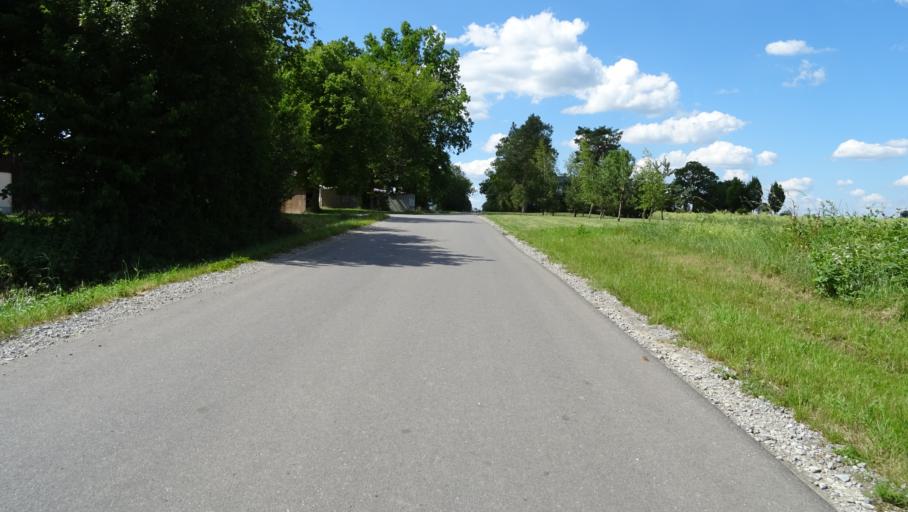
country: DE
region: Baden-Wuerttemberg
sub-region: Karlsruhe Region
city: Adelsheim
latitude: 49.3894
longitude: 9.3718
